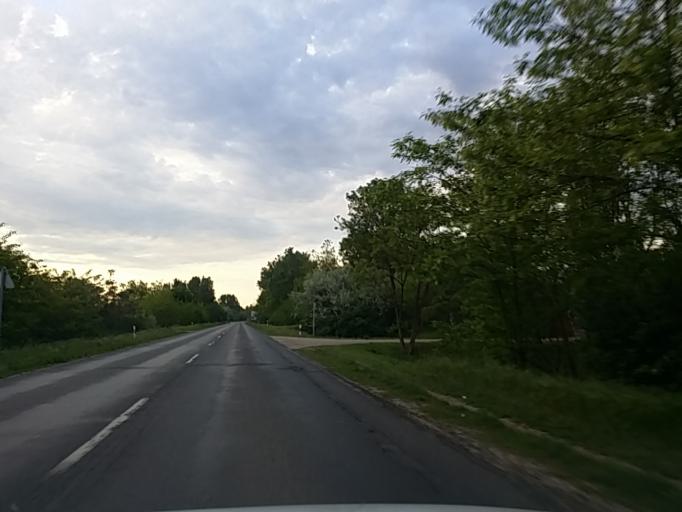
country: HU
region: Bacs-Kiskun
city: Lajosmizse
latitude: 46.9969
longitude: 19.6003
